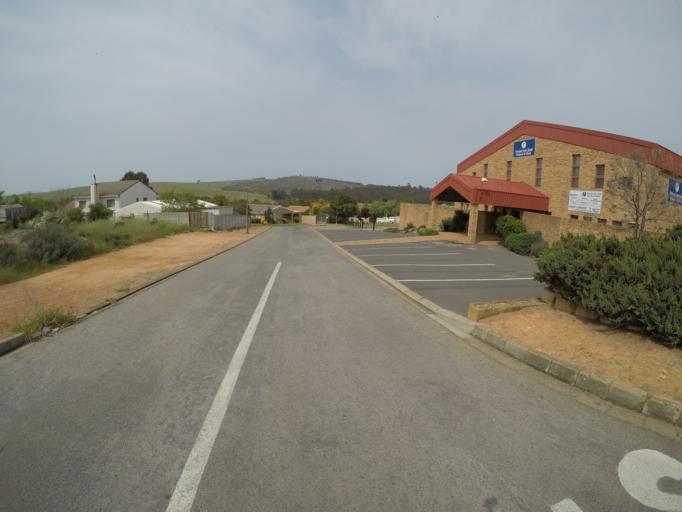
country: ZA
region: Western Cape
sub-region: West Coast District Municipality
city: Malmesbury
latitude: -33.4599
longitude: 18.7415
